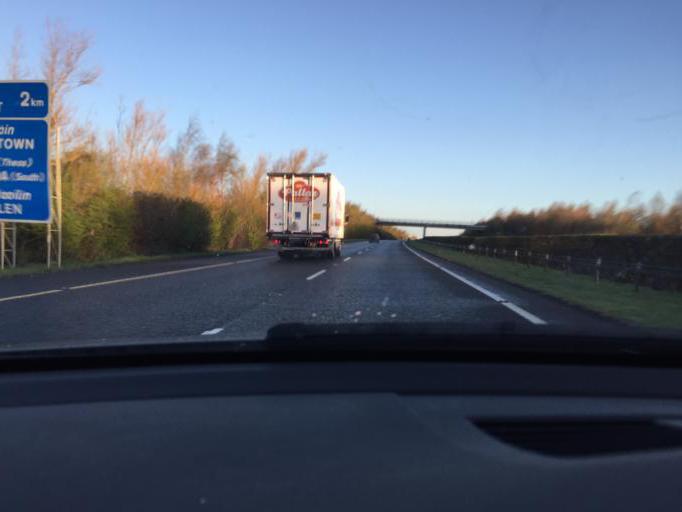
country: IE
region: Leinster
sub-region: An Mhi
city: Stamullin
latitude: 53.6150
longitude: -6.2422
